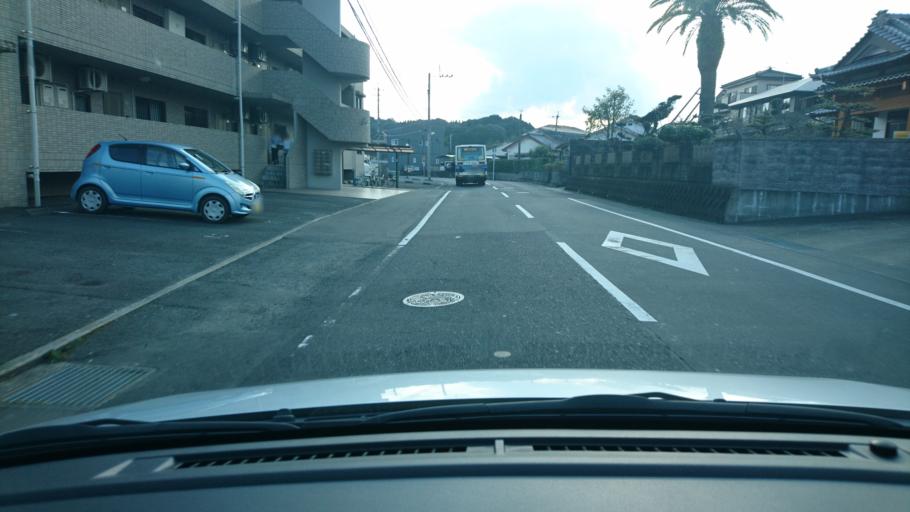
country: JP
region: Miyazaki
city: Miyazaki-shi
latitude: 31.8712
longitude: 131.4041
